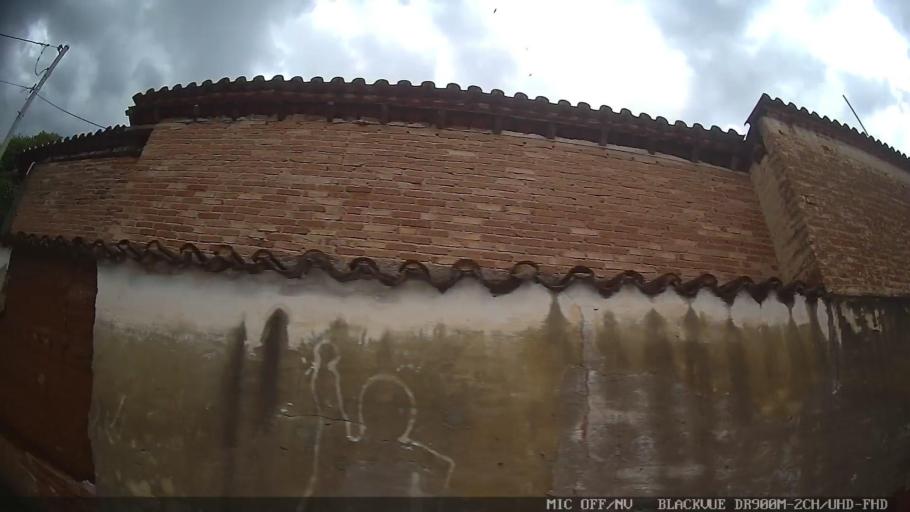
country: BR
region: Sao Paulo
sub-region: Amparo
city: Amparo
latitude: -22.6998
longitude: -46.7662
